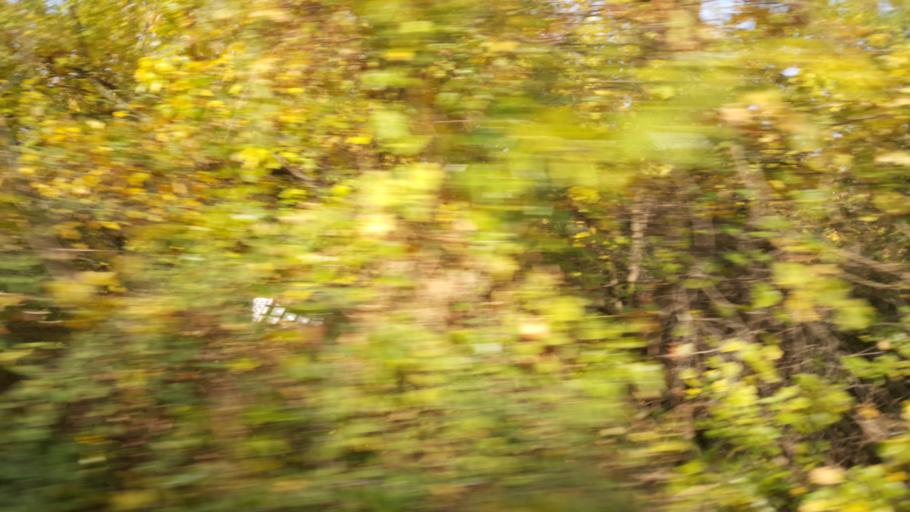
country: TR
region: Eskisehir
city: Mihaliccik
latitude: 39.9883
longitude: 31.3507
